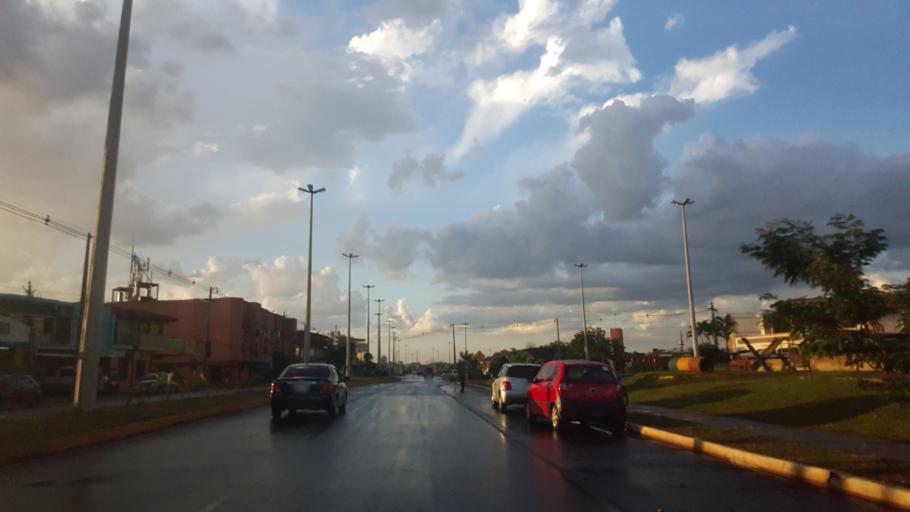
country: PY
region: Itapua
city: Encarnacion
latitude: -27.3566
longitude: -55.8586
